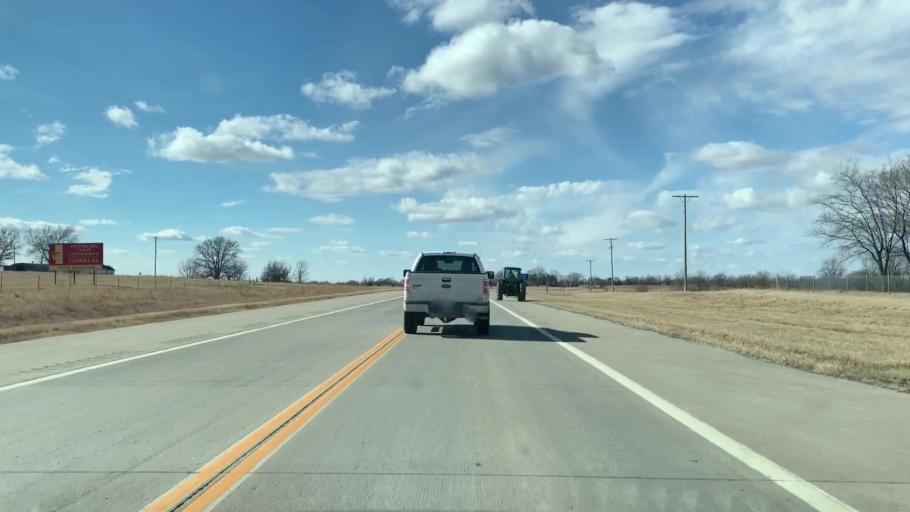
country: US
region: Kansas
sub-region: Labette County
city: Parsons
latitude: 37.3405
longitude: -95.1748
